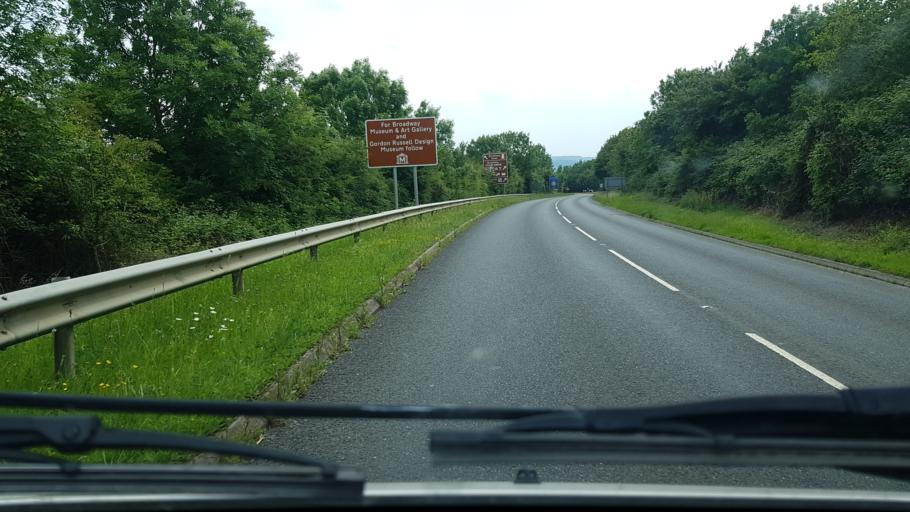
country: GB
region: England
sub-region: Worcestershire
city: Broadway
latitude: 52.0525
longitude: -1.8796
